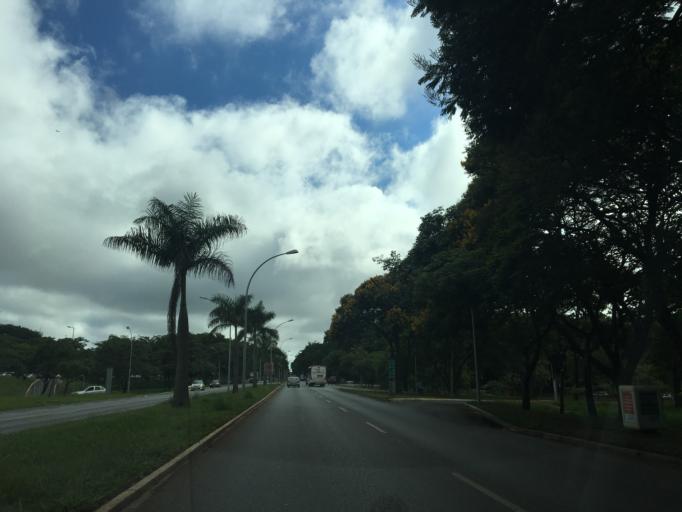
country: BR
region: Federal District
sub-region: Brasilia
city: Brasilia
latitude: -15.8302
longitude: -47.9179
